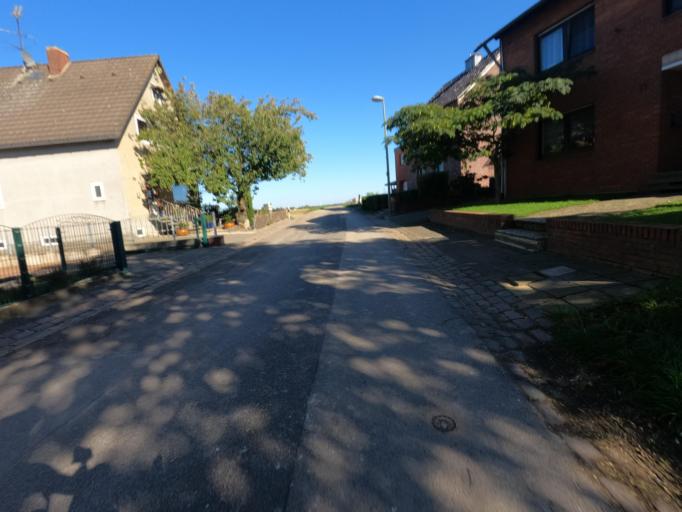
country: DE
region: North Rhine-Westphalia
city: Erkelenz
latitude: 51.0753
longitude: 6.3489
